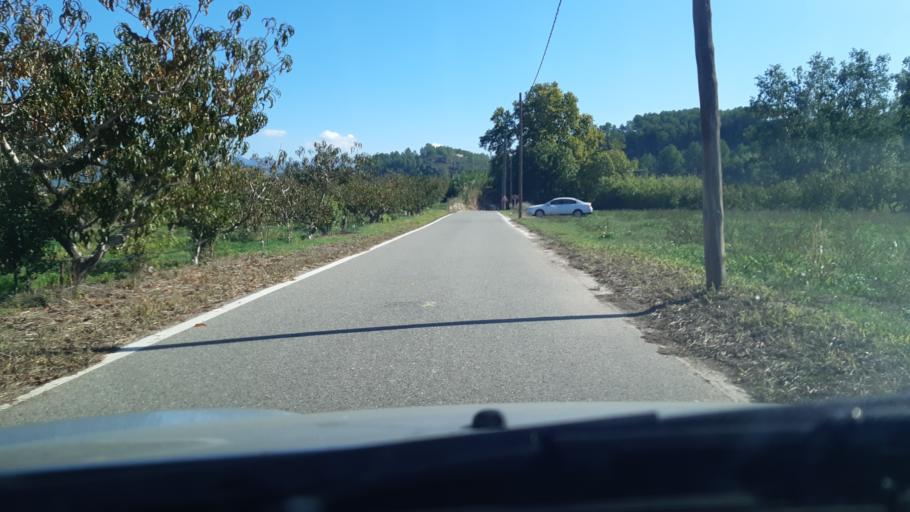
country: ES
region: Catalonia
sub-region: Provincia de Tarragona
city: Miravet
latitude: 41.0337
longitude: 0.6070
